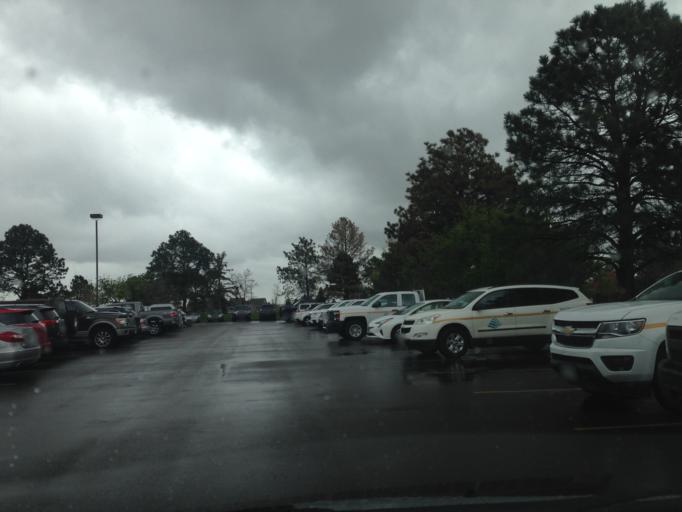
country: US
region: Colorado
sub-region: Adams County
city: Westminster
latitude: 39.8621
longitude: -105.0472
